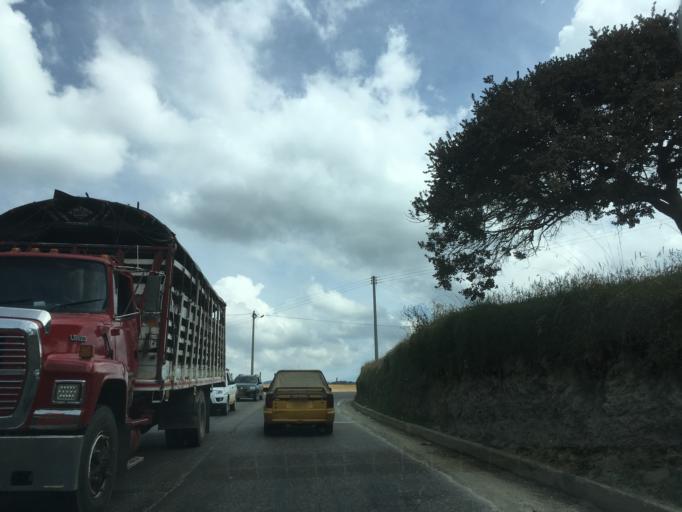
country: CO
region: Boyaca
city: Sogamoso
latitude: 5.6390
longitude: -72.9210
